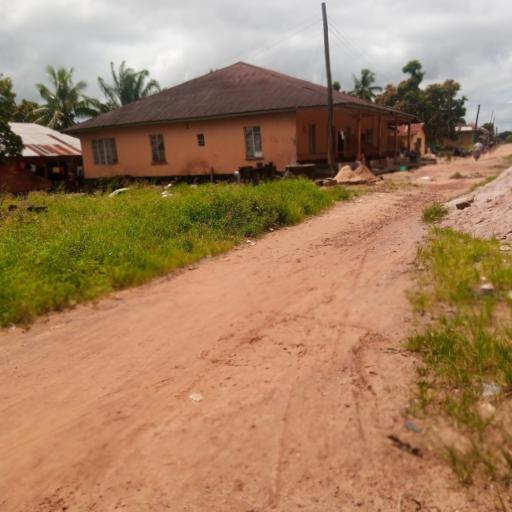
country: SL
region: Eastern Province
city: Kenema
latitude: 7.8910
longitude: -11.1860
